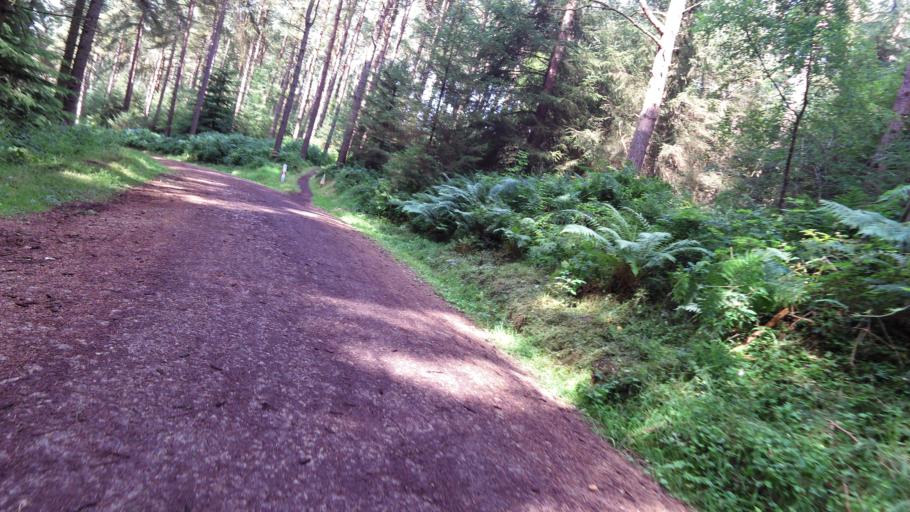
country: GB
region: England
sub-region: North Yorkshire
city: Thornton Dale
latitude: 54.2973
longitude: -0.6326
